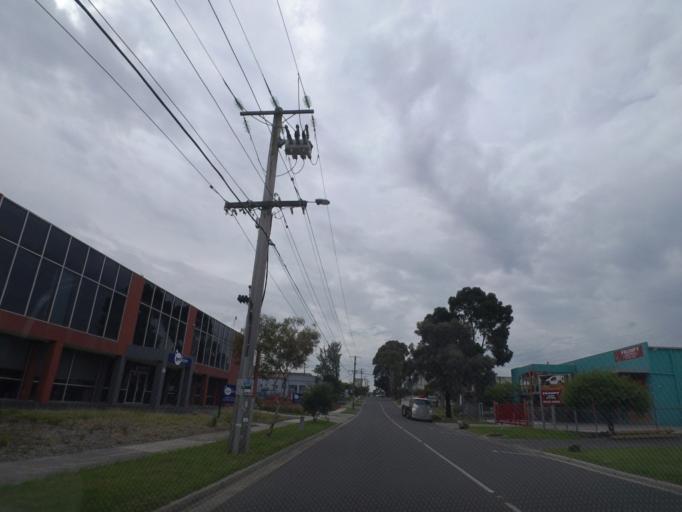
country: AU
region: Victoria
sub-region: Knox
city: Bayswater
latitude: -37.8415
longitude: 145.2795
